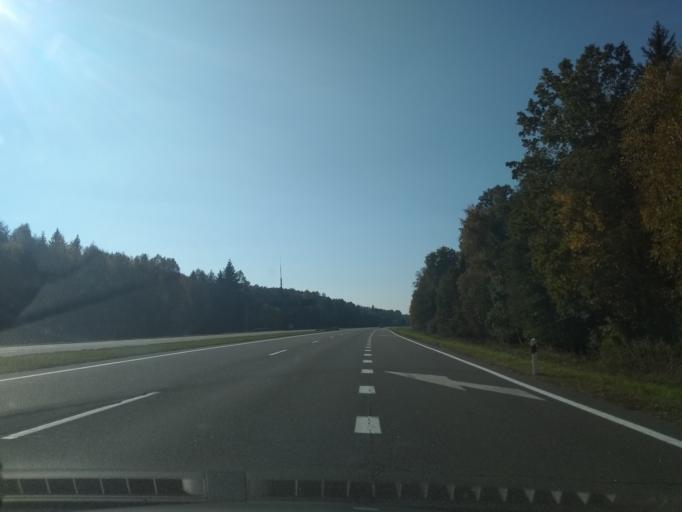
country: BY
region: Brest
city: Ivatsevichy
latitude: 52.8525
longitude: 25.6417
